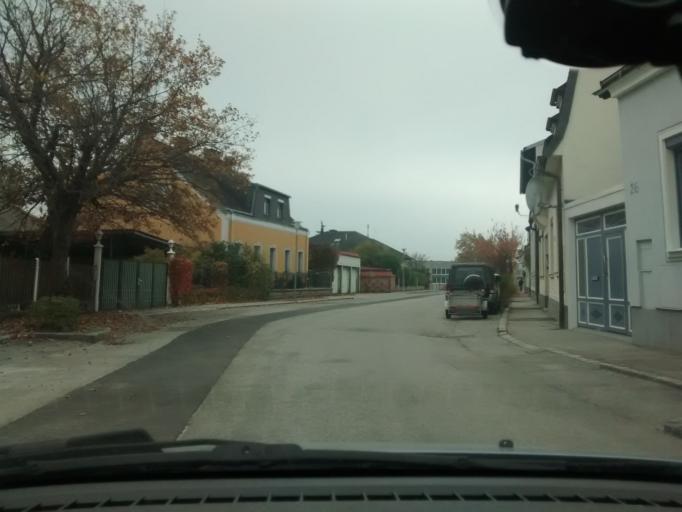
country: AT
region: Lower Austria
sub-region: Politischer Bezirk Modling
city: Guntramsdorf
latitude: 48.0447
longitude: 16.3077
